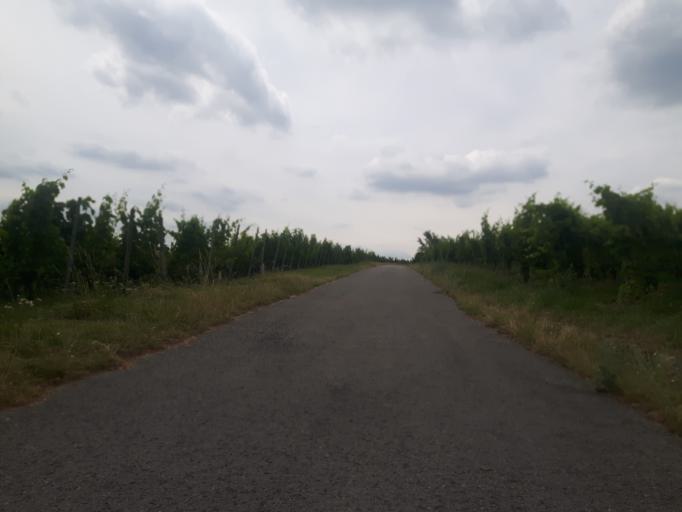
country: DE
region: Baden-Wuerttemberg
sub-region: Regierungsbezirk Stuttgart
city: Bonnigheim
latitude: 49.0394
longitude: 9.0694
